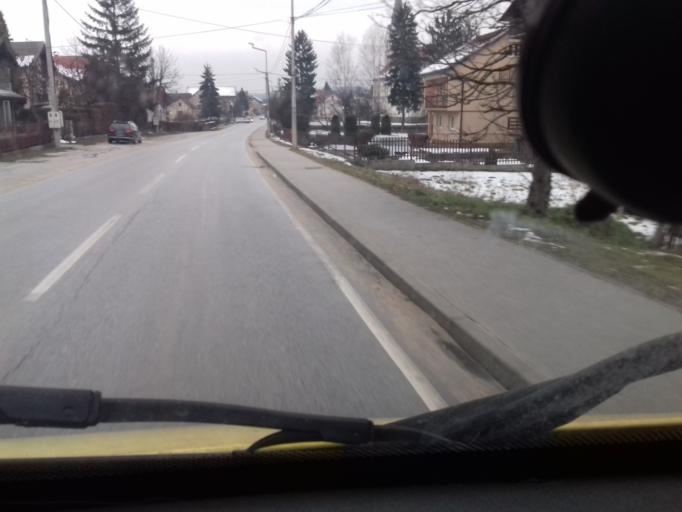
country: BA
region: Federation of Bosnia and Herzegovina
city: Vitez
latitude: 44.1615
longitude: 17.7815
